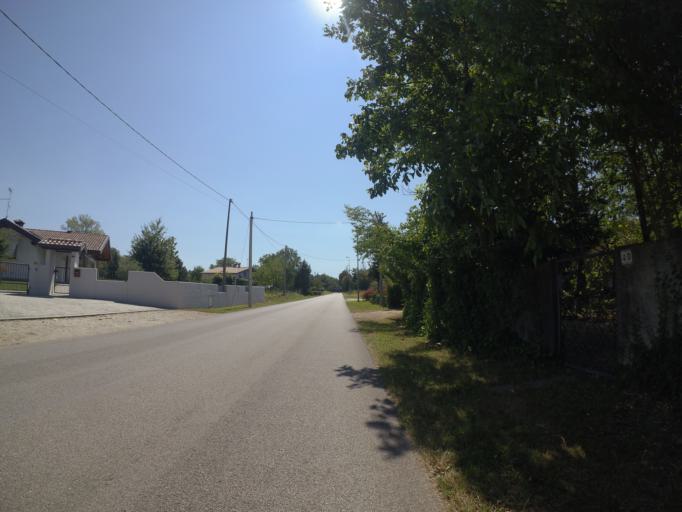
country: IT
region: Friuli Venezia Giulia
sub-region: Provincia di Udine
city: Lestizza
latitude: 45.9657
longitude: 13.1625
